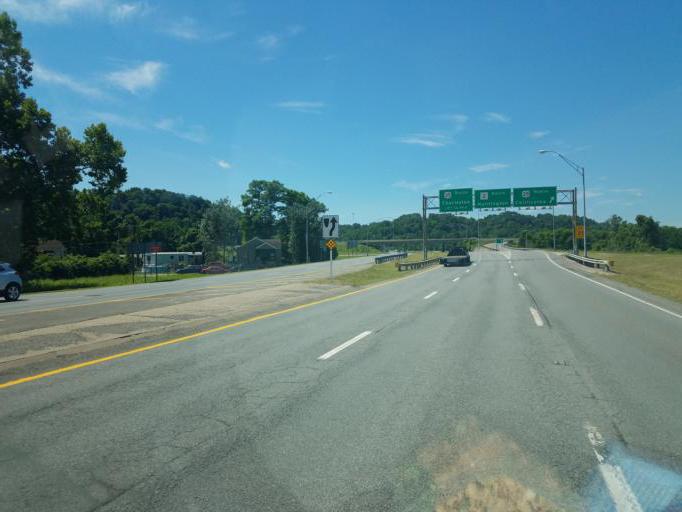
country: US
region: West Virginia
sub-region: Mason County
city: Point Pleasant
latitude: 38.8342
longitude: -82.1412
